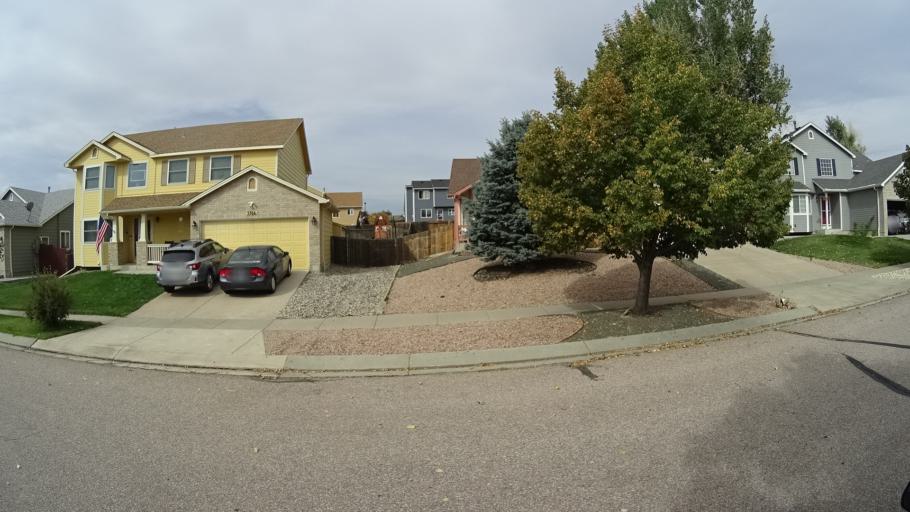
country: US
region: Colorado
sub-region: El Paso County
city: Cimarron Hills
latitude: 38.9160
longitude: -104.7106
